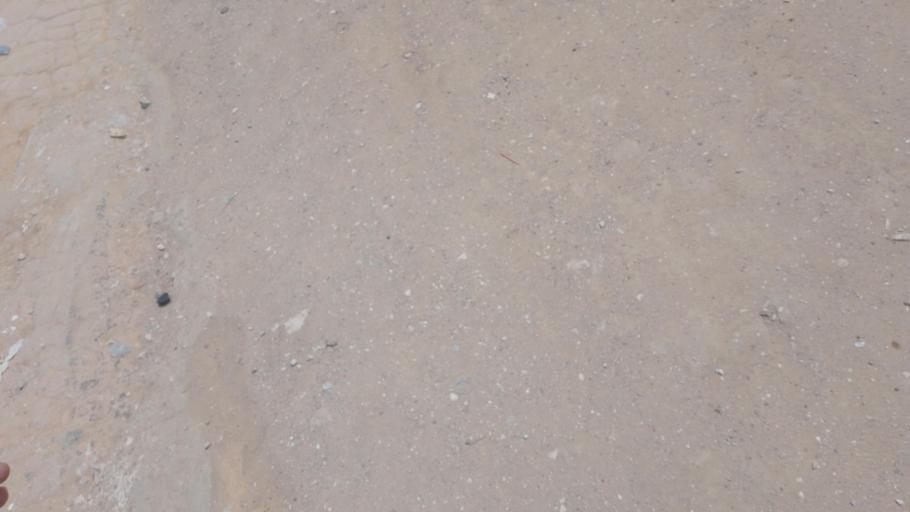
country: ZM
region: Lusaka
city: Lusaka
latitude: -15.3944
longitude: 28.3785
